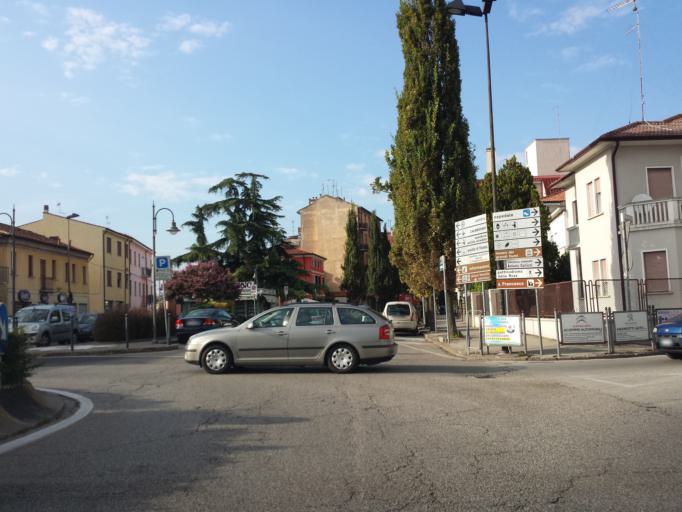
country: IT
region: Veneto
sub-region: Provincia di Rovigo
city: Rovigo
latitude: 45.0639
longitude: 11.7942
